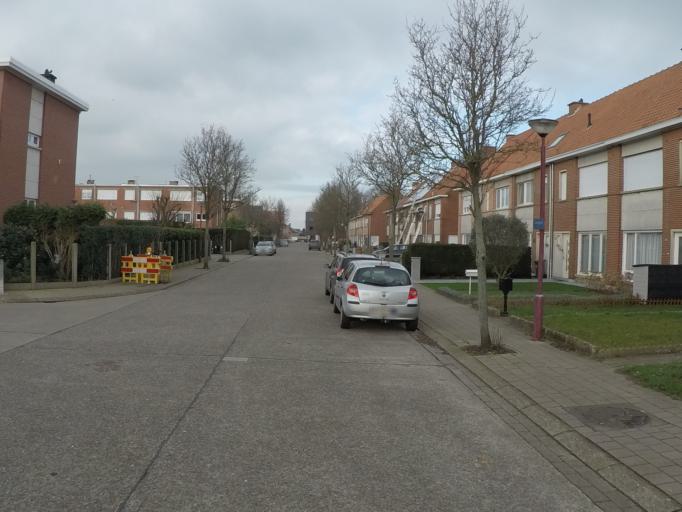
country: BE
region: Flanders
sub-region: Provincie Antwerpen
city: Kapellen
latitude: 51.3110
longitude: 4.4019
